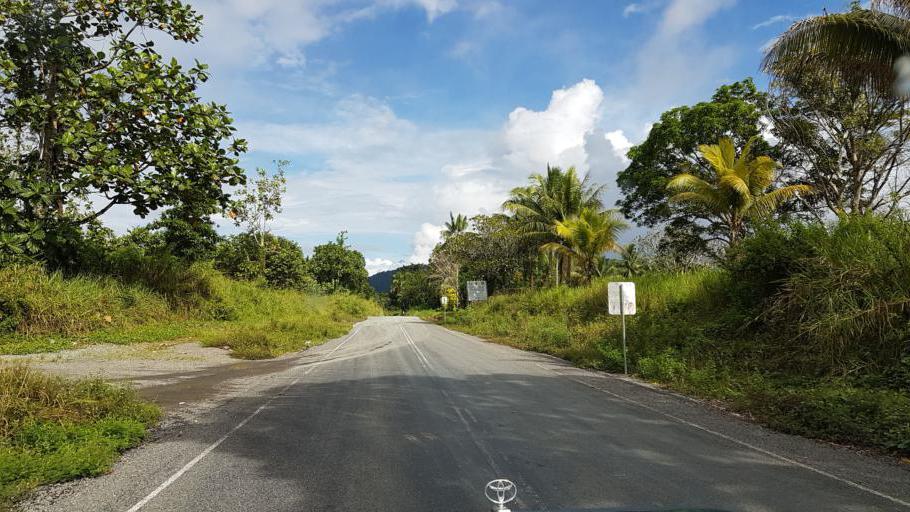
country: PG
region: Northern Province
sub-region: Sohe
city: Kokoda
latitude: -8.9053
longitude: 147.9783
